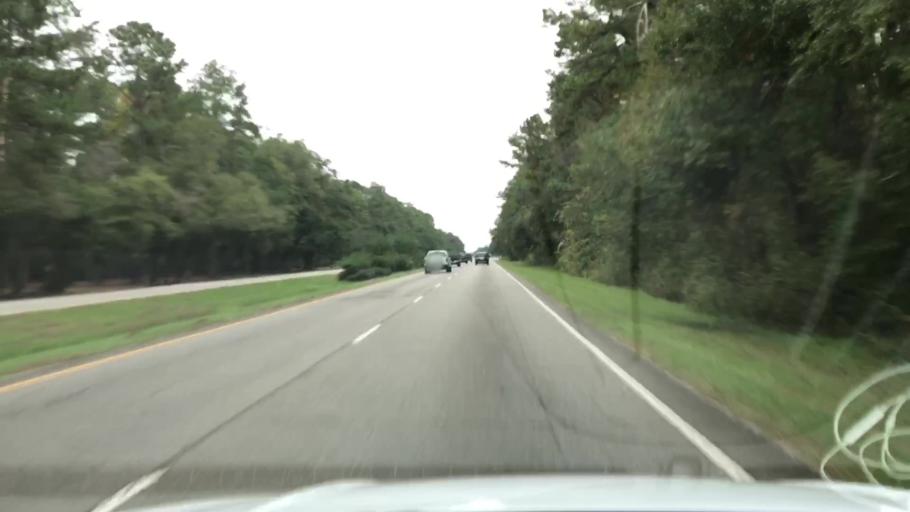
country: US
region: South Carolina
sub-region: Georgetown County
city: Murrells Inlet
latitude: 33.5187
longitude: -79.0696
